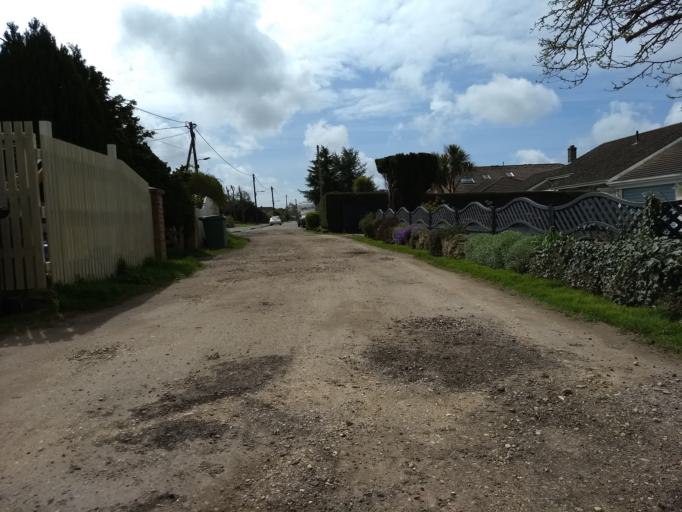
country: GB
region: England
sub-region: Isle of Wight
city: East Cowes
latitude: 50.7318
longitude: -1.2368
